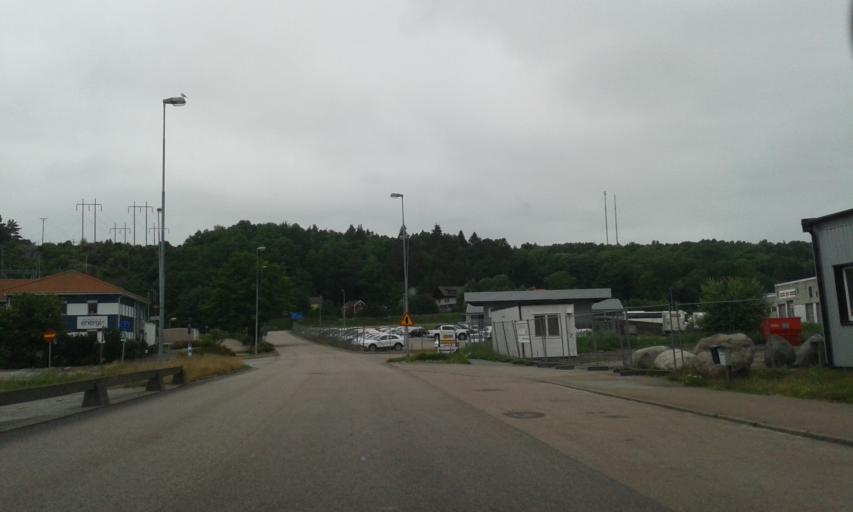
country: SE
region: Vaestra Goetaland
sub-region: Kungalvs Kommun
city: Kungalv
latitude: 57.8775
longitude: 11.9806
